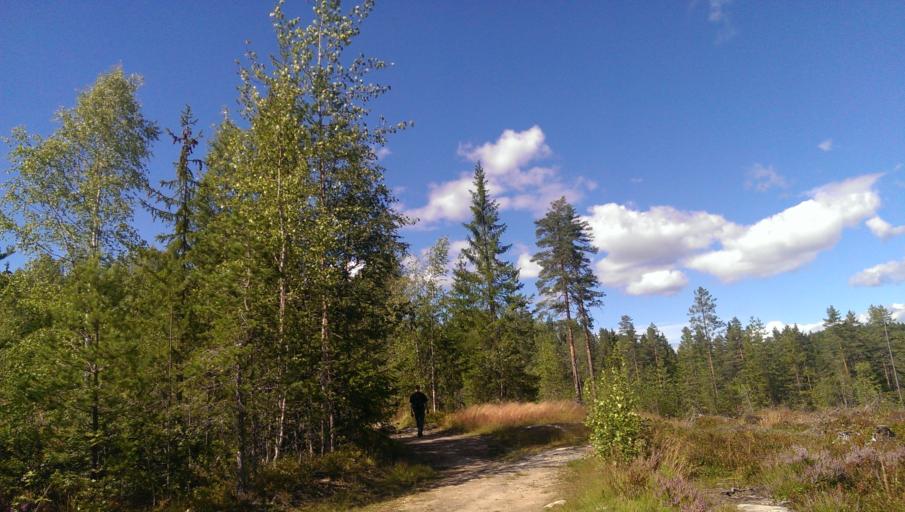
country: NO
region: Buskerud
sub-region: Kongsberg
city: Kongsberg
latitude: 59.6676
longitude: 9.6152
